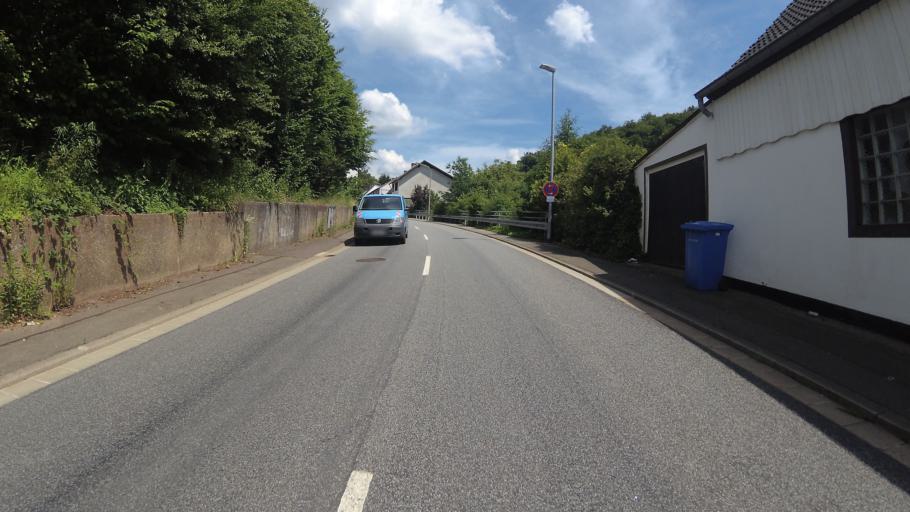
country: DE
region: Saarland
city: Homburg
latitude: 49.2993
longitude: 7.3726
